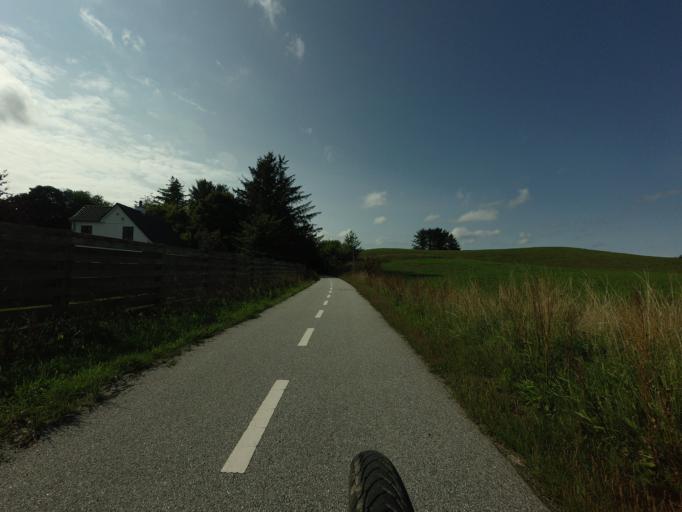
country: DK
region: North Denmark
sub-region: Hjorring Kommune
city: Hjorring
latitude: 57.5145
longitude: 10.0363
